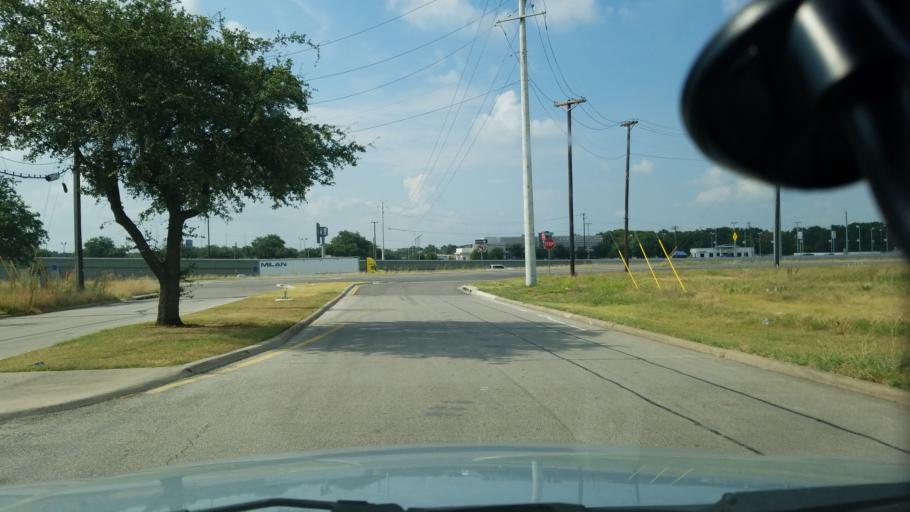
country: US
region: Texas
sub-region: Dallas County
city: Irving
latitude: 32.8383
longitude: -96.9224
